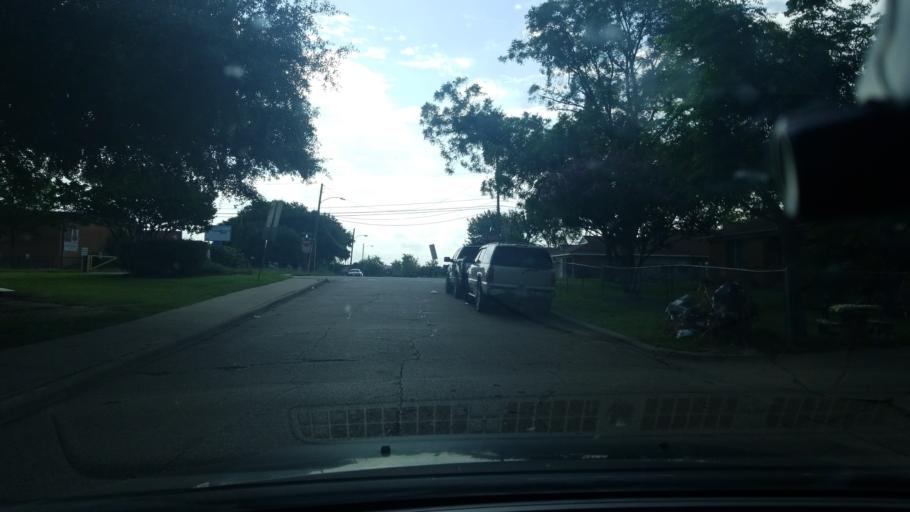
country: US
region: Texas
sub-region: Dallas County
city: Balch Springs
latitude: 32.7507
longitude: -96.6704
